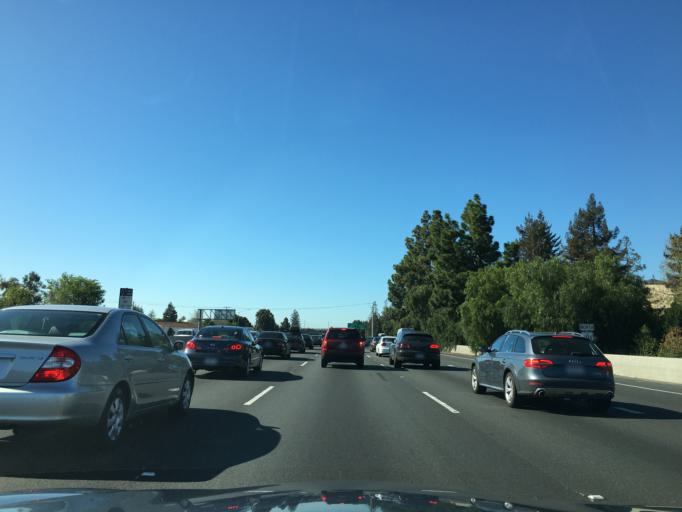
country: US
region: California
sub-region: Santa Clara County
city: Mountain View
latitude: 37.4176
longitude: -122.0875
